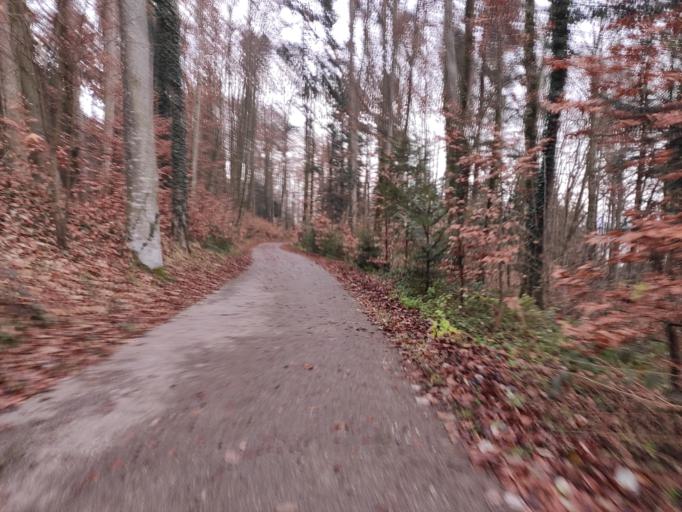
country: AT
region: Salzburg
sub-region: Politischer Bezirk Salzburg-Umgebung
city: Berndorf bei Salzburg
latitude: 47.9895
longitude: 13.0833
